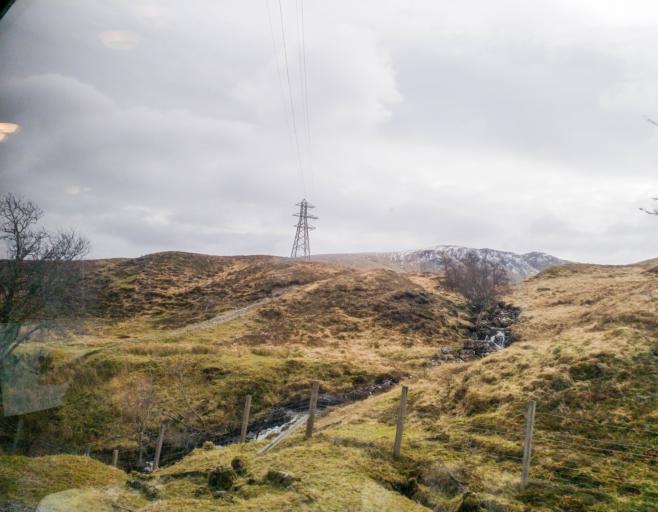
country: GB
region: Scotland
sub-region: Highland
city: Spean Bridge
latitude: 56.5942
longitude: -4.6345
